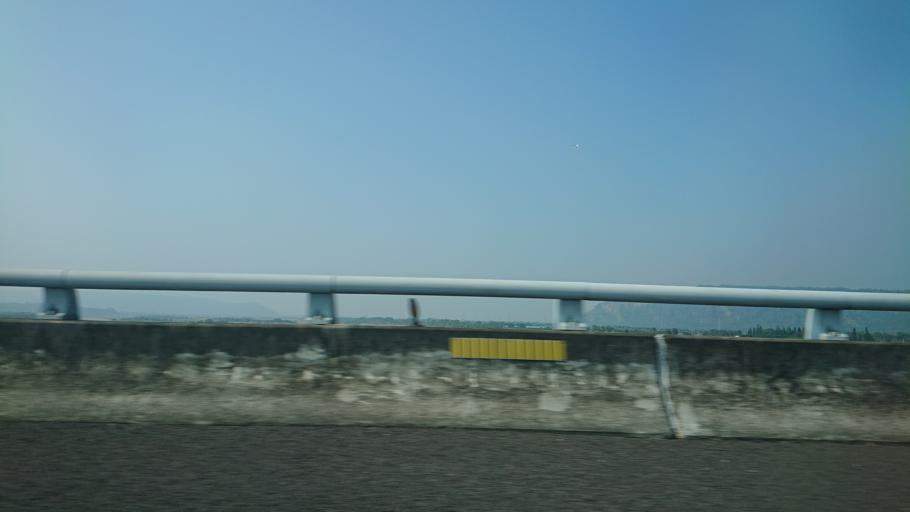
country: TW
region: Taiwan
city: Lugu
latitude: 23.8047
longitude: 120.6977
